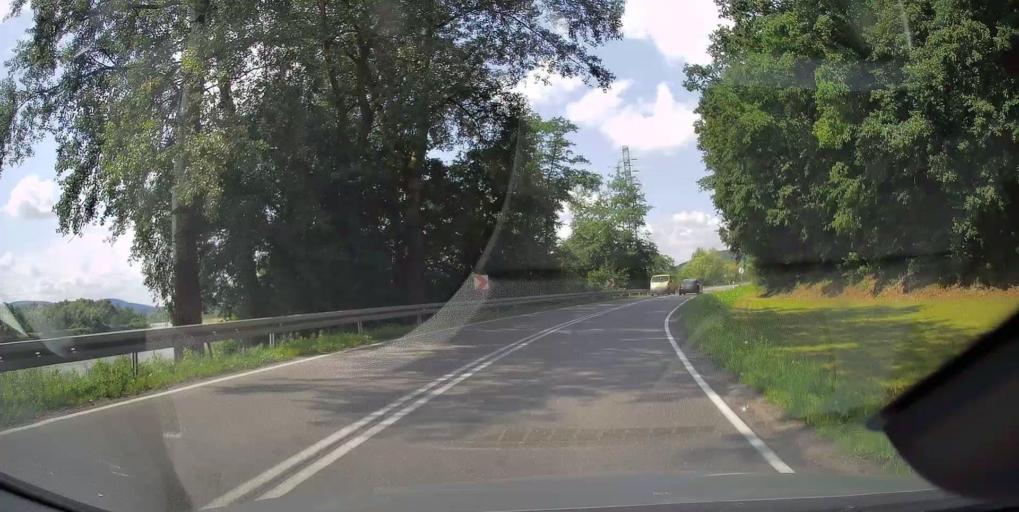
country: PL
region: Lesser Poland Voivodeship
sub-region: Powiat tarnowski
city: Zakliczyn
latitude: 49.8764
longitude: 20.8289
